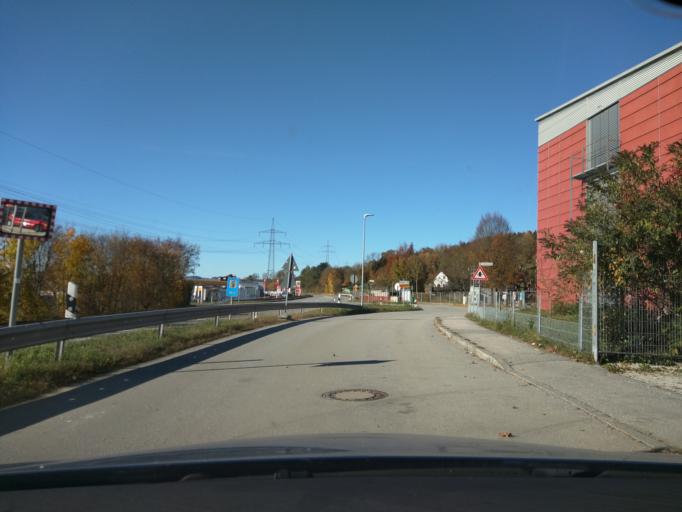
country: DE
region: Bavaria
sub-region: Lower Bavaria
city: Passau
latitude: 48.5817
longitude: 13.4102
